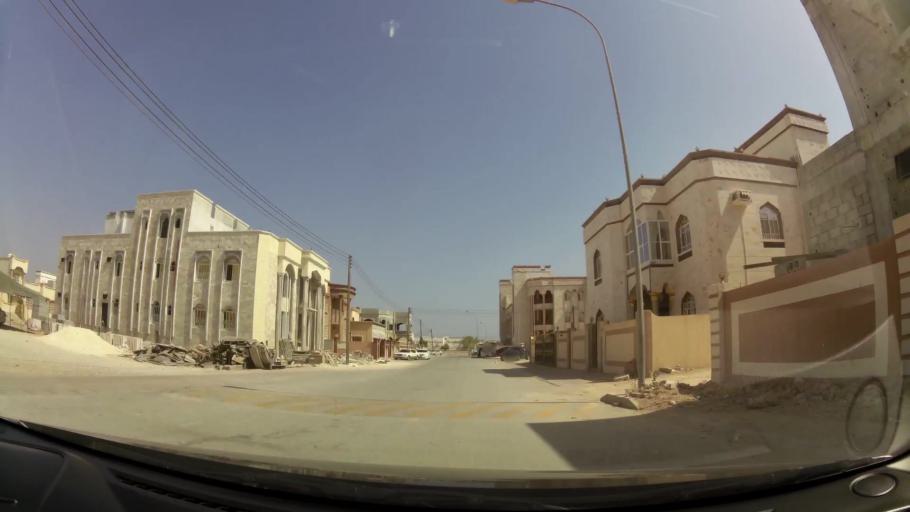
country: OM
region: Zufar
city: Salalah
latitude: 17.0476
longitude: 54.1571
